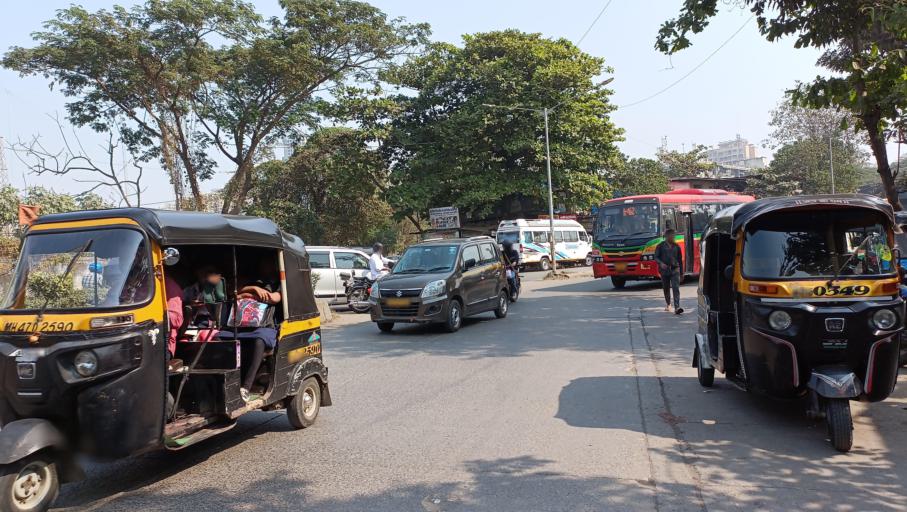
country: IN
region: Maharashtra
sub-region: Mumbai Suburban
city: Borivli
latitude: 19.2559
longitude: 72.8695
